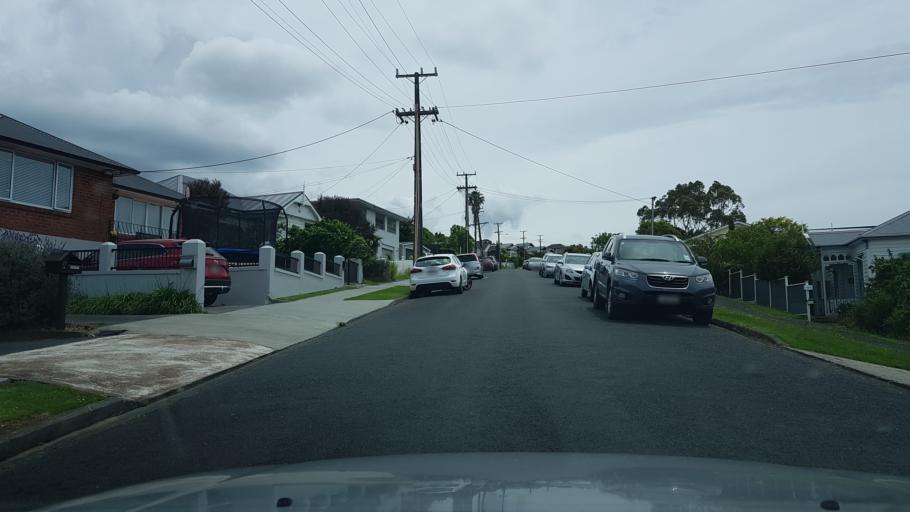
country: NZ
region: Auckland
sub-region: Auckland
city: North Shore
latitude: -36.8148
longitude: 174.7226
